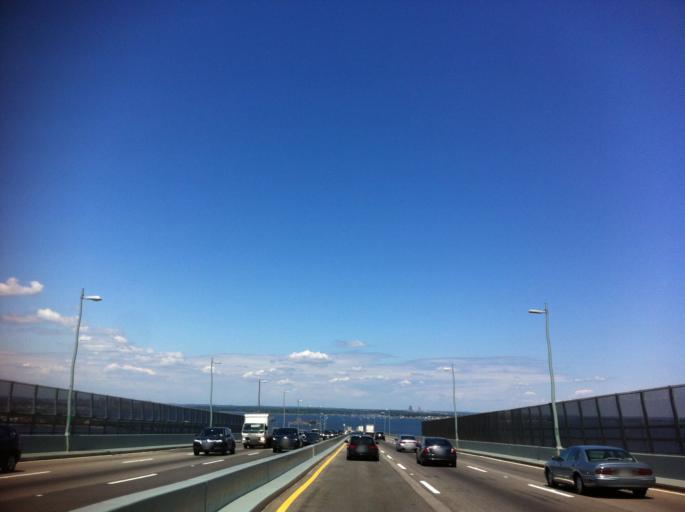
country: US
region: New York
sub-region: Nassau County
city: East Atlantic Beach
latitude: 40.8064
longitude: -73.7937
